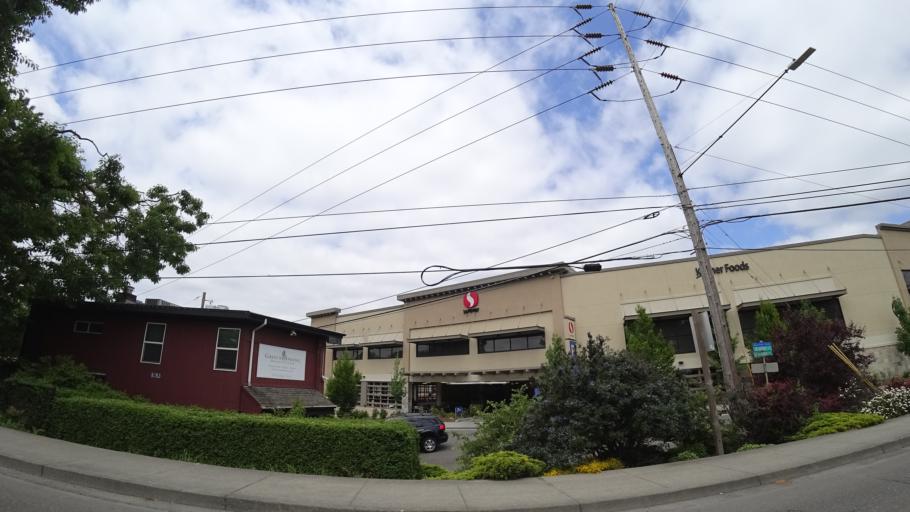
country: US
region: Oregon
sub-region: Clackamas County
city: Lake Oswego
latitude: 45.4653
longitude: -122.6985
